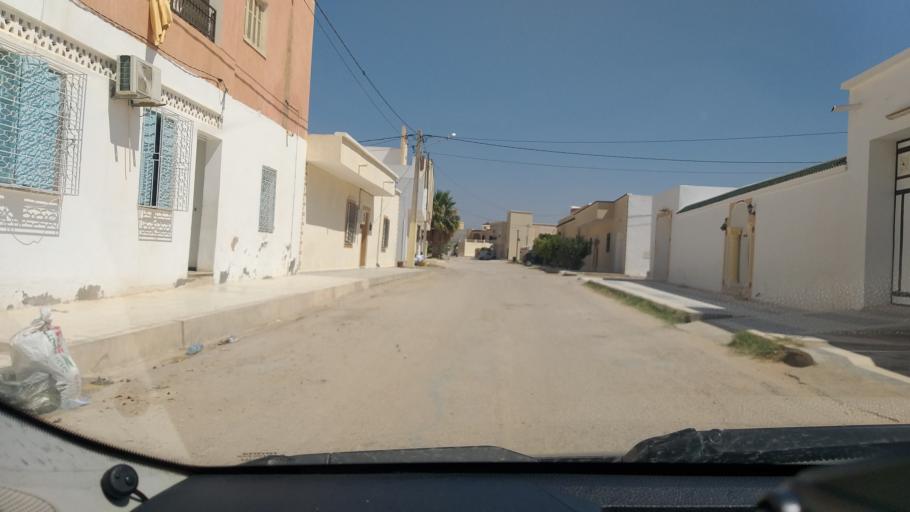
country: TN
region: Al Mahdiyah
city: El Jem
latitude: 35.2895
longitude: 10.7174
